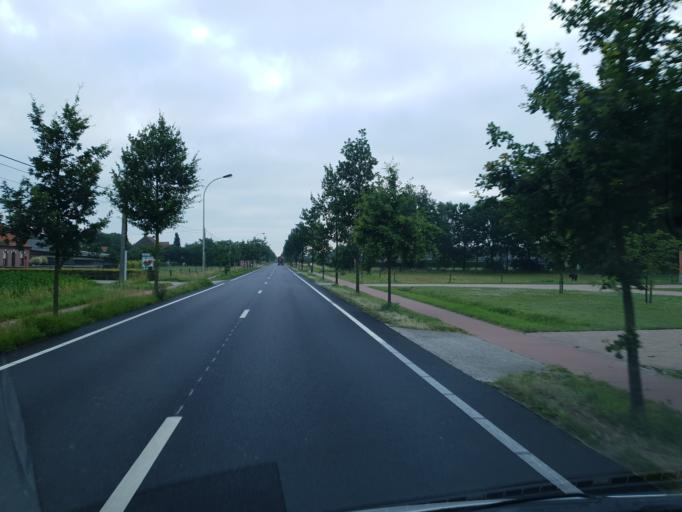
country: BE
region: Flanders
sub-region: Provincie Antwerpen
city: Rijkevorsel
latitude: 51.3694
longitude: 4.7110
